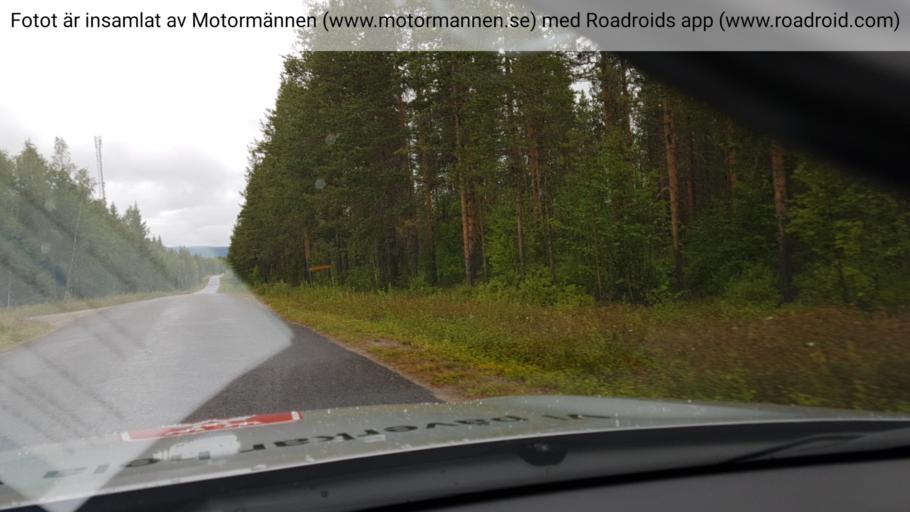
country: SE
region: Norrbotten
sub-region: Alvsbyns Kommun
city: AElvsbyn
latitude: 66.0779
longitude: 20.9166
